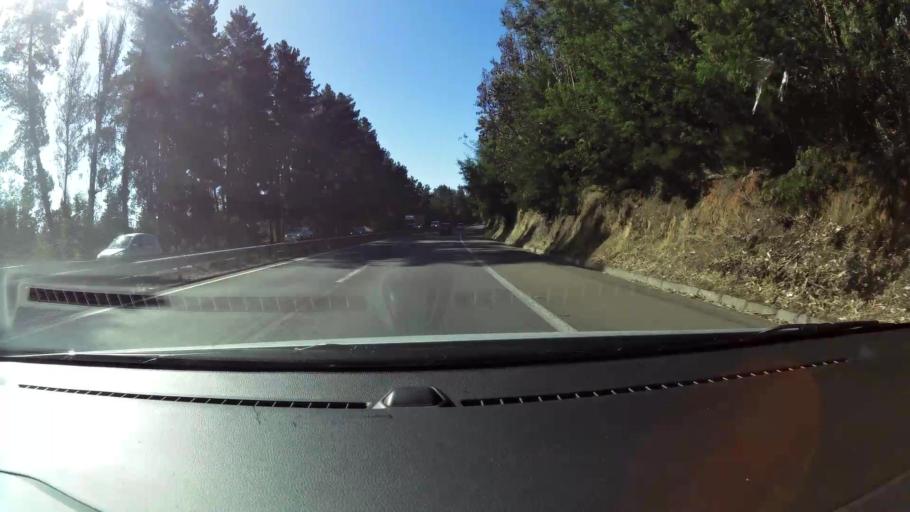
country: CL
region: Valparaiso
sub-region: Provincia de Valparaiso
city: Vina del Mar
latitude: -33.1527
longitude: -71.5568
